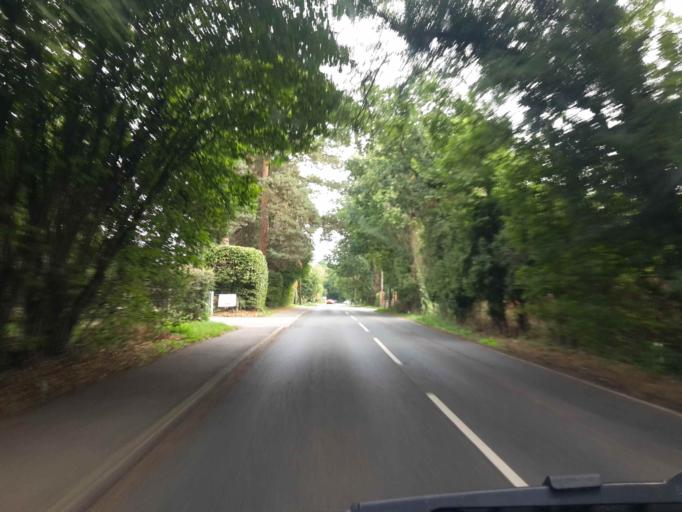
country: GB
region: England
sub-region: Wokingham
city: Wokingham
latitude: 51.4027
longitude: -0.8170
